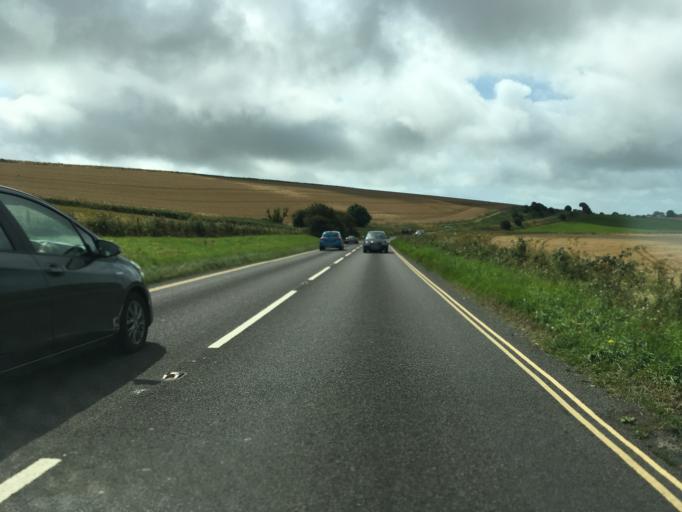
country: GB
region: England
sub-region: Brighton and Hove
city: Rottingdean
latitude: 50.8472
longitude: -0.0707
